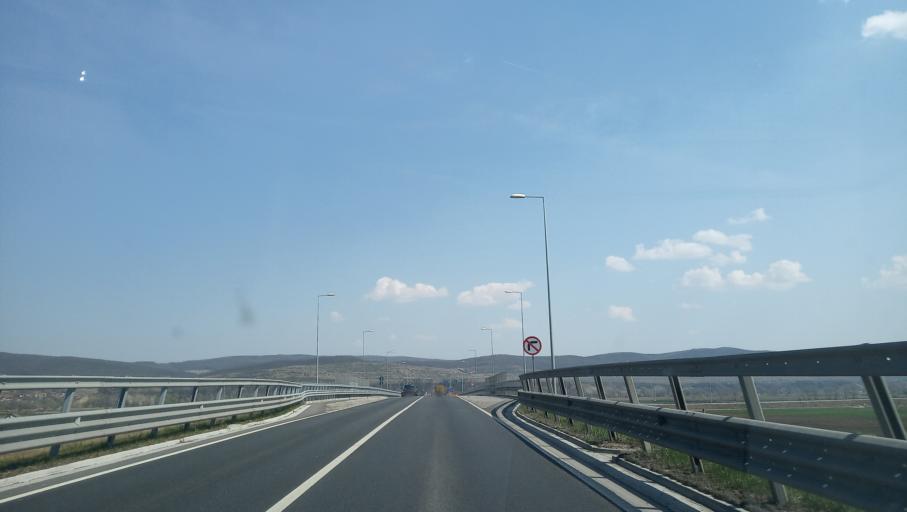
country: RO
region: Alba
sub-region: Municipiul Aiud
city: Aiud
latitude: 46.3289
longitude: 23.7225
